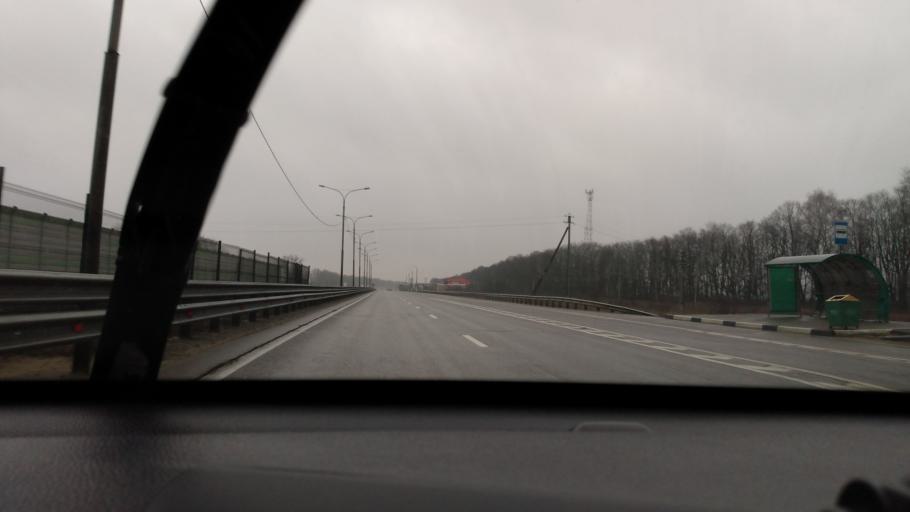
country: RU
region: Tula
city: Shvartsevskiy
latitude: 54.1109
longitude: 38.0570
